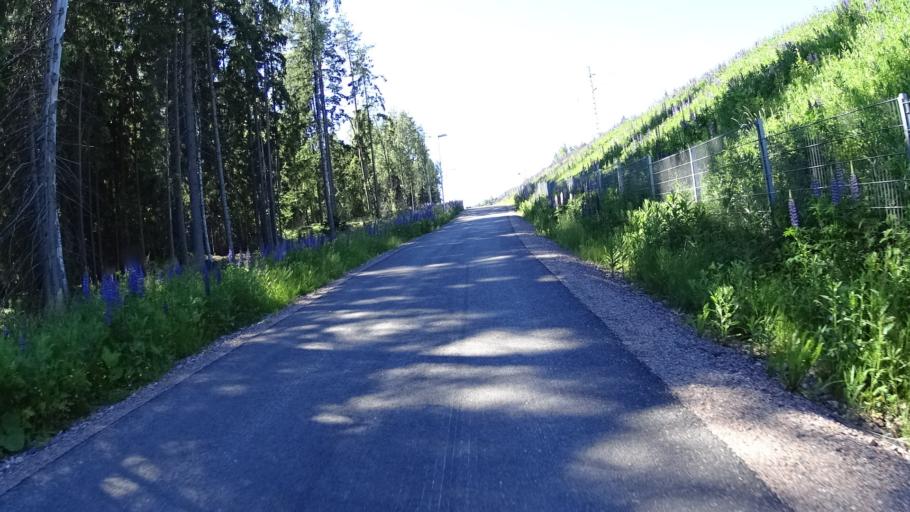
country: FI
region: Uusimaa
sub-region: Helsinki
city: Kilo
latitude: 60.3052
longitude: 24.8424
